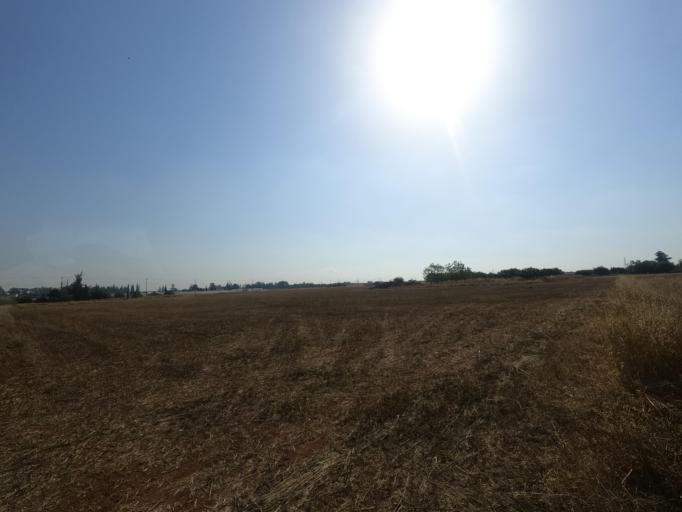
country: CY
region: Ammochostos
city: Avgorou
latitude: 35.0391
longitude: 33.8520
